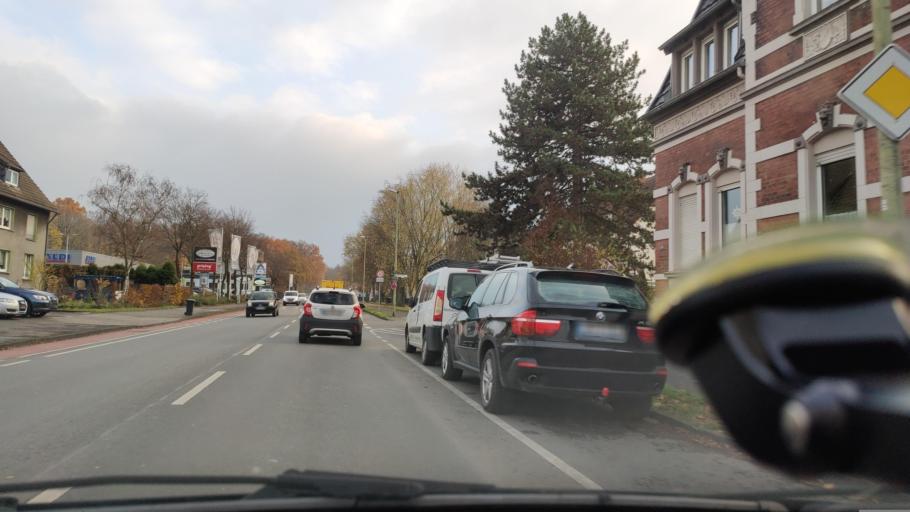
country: DE
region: North Rhine-Westphalia
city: Lunen
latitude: 51.5926
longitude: 7.5352
